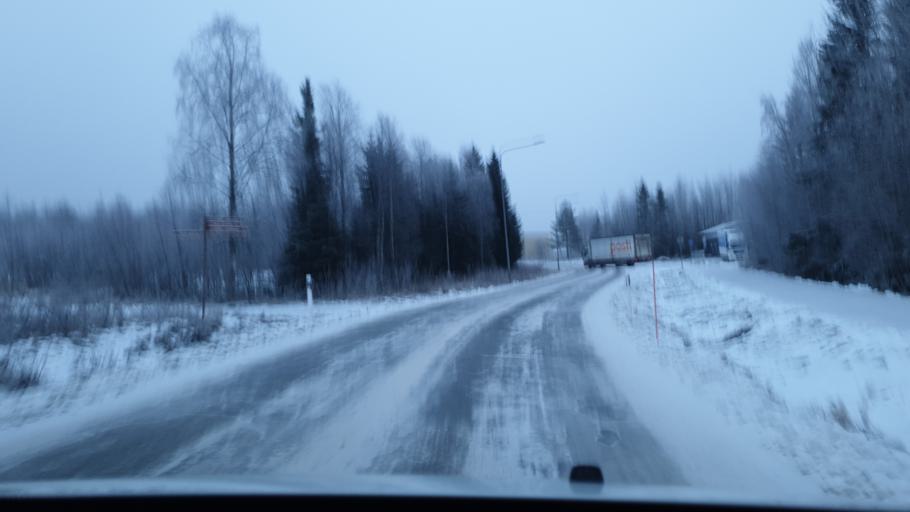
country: FI
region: Lapland
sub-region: Kemi-Tornio
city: Kemi
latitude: 65.7365
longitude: 24.6087
